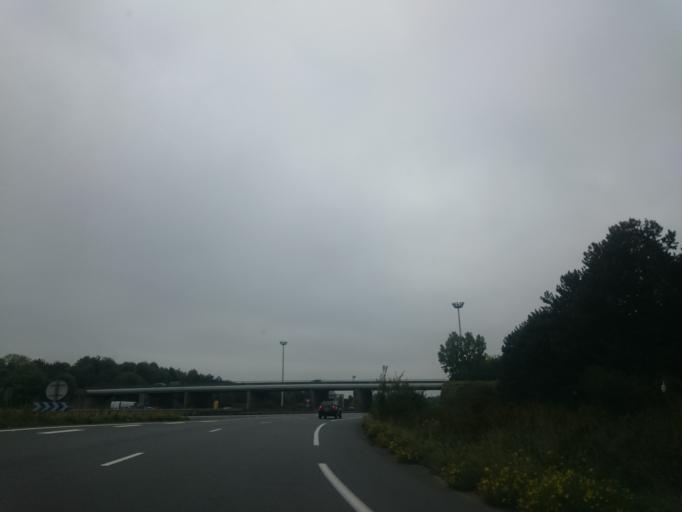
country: FR
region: Ile-de-France
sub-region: Departement de l'Essonne
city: Ris-Orangis
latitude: 48.6351
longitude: 2.4028
